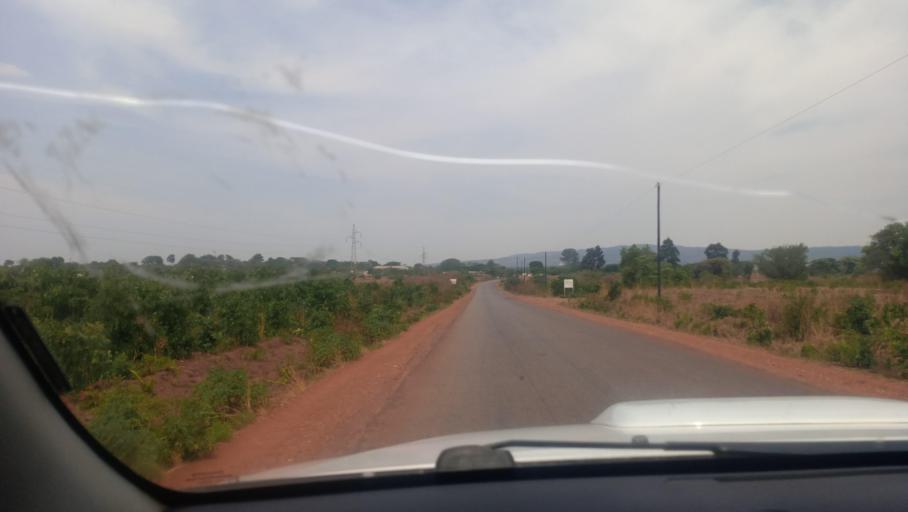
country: ZM
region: Northern
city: Mpika
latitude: -11.8330
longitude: 31.4170
